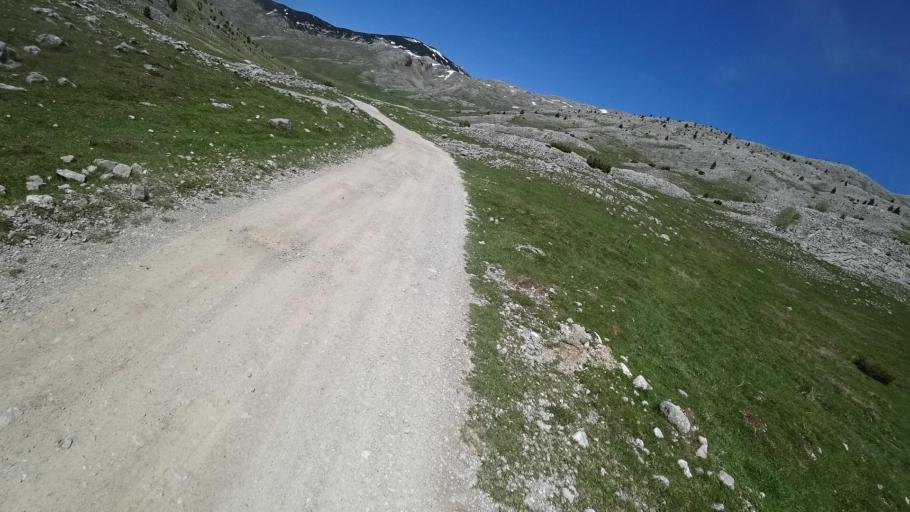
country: BA
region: Federation of Bosnia and Herzegovina
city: Gracanica
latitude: 43.6873
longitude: 18.2093
